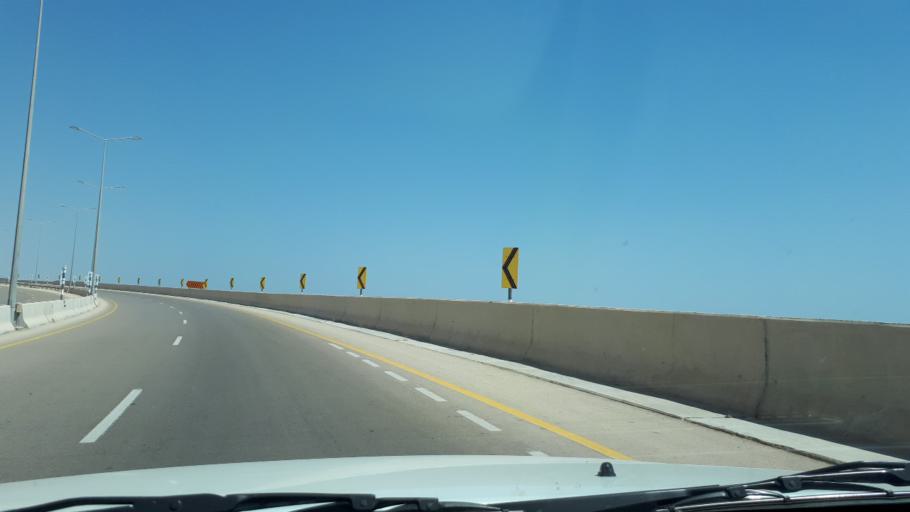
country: OM
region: Ash Sharqiyah
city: Sur
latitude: 22.8200
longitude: 59.2617
